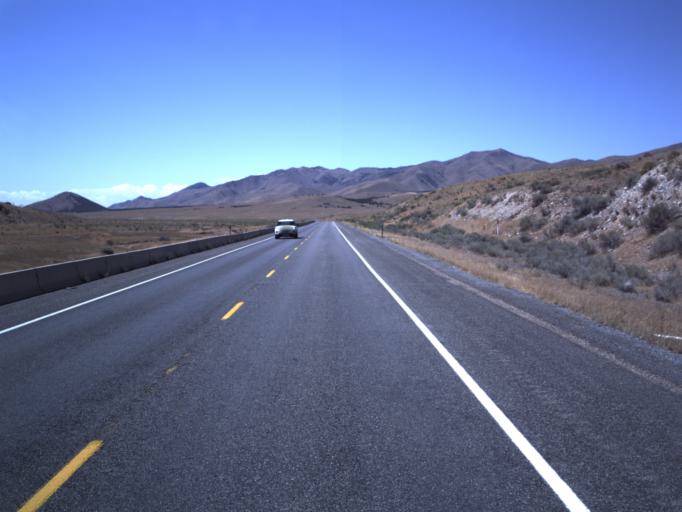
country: US
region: Utah
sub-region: Juab County
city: Nephi
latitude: 39.6373
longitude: -112.0984
